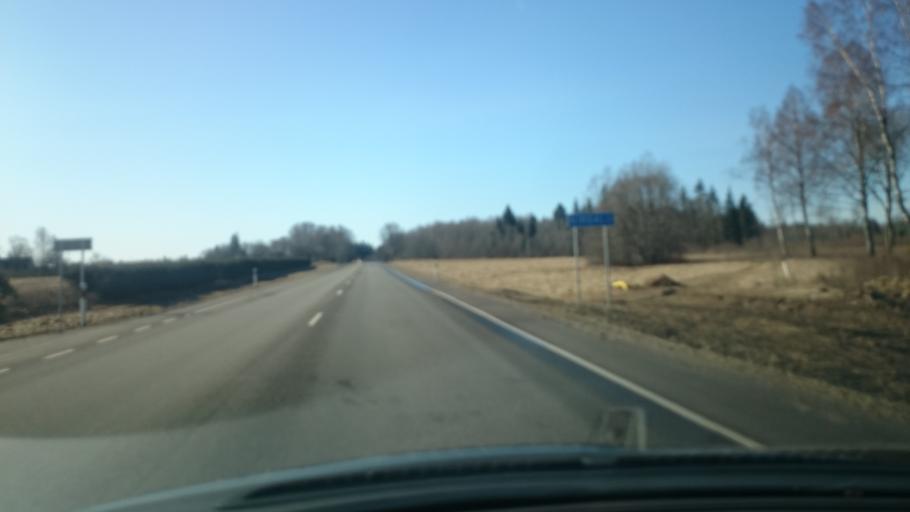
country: EE
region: Harju
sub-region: Saku vald
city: Saku
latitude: 59.2608
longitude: 24.7409
